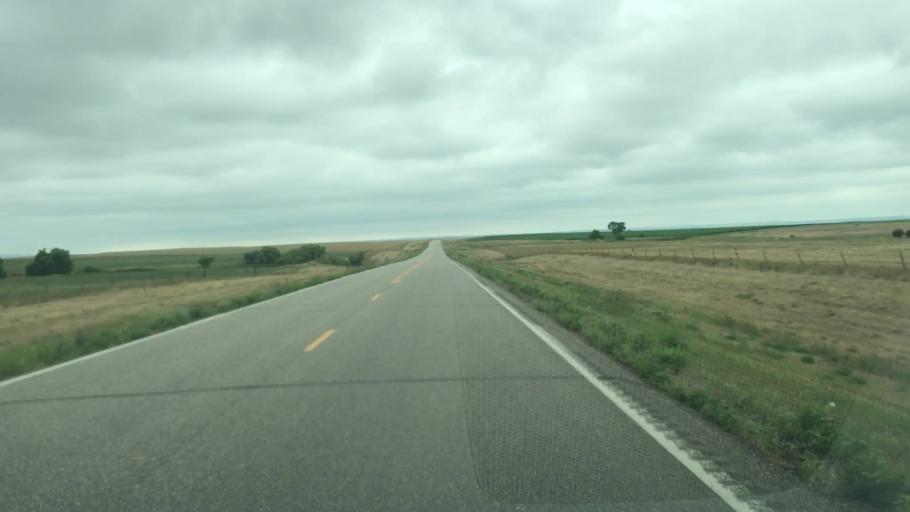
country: US
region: South Dakota
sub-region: Jackson County
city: Kadoka
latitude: 43.8188
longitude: -101.5224
